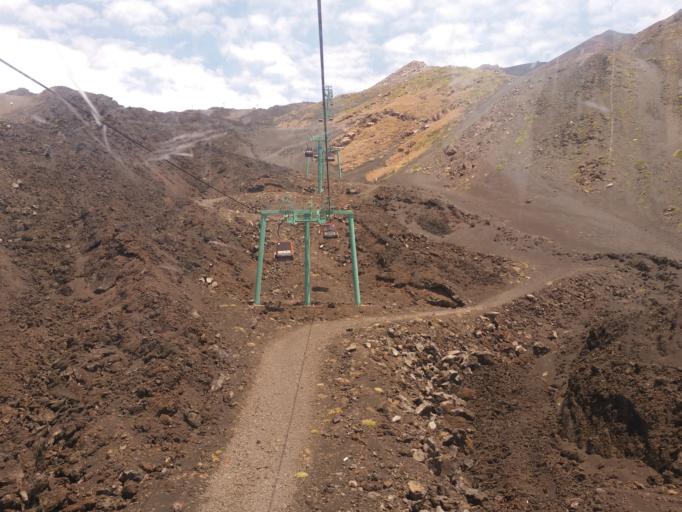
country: IT
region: Sicily
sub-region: Catania
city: Ragalna
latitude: 37.7091
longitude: 14.9994
